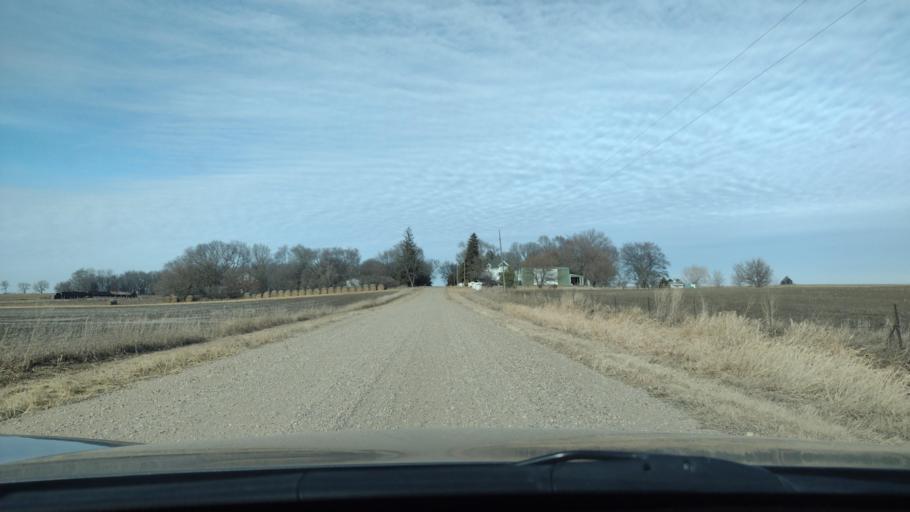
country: US
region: South Dakota
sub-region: Union County
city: Beresford
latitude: 42.9591
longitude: -96.8055
